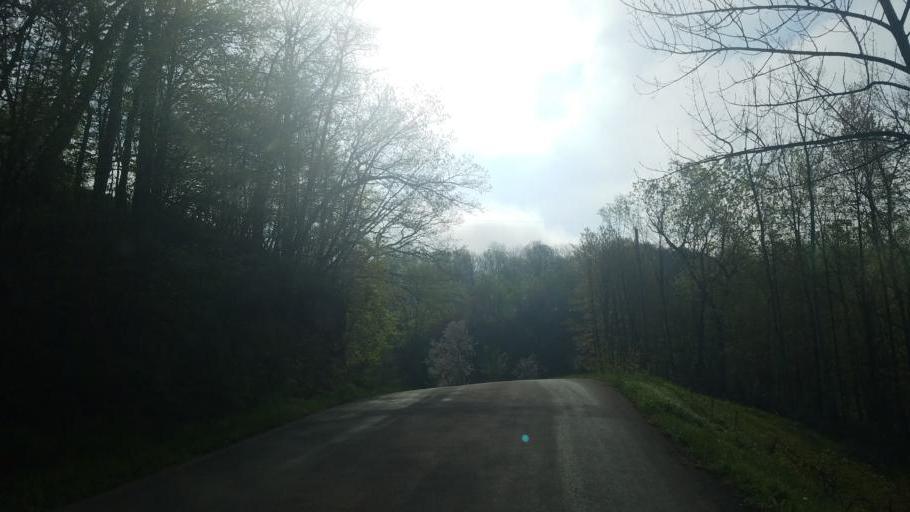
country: US
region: Wisconsin
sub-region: Vernon County
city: Hillsboro
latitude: 43.6261
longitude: -90.4338
